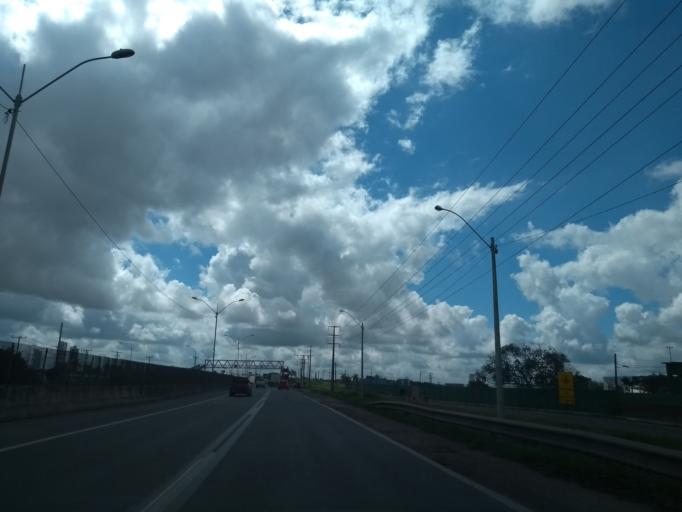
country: BR
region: Bahia
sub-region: Feira De Santana
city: Feira de Santana
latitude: -12.2760
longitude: -38.9384
